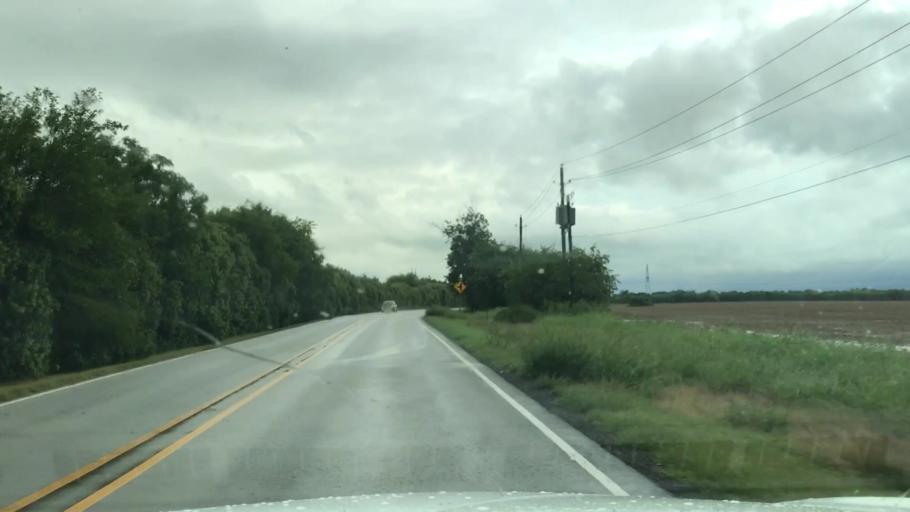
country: US
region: Texas
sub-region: Collin County
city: Lucas
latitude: 33.0697
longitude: -96.5702
